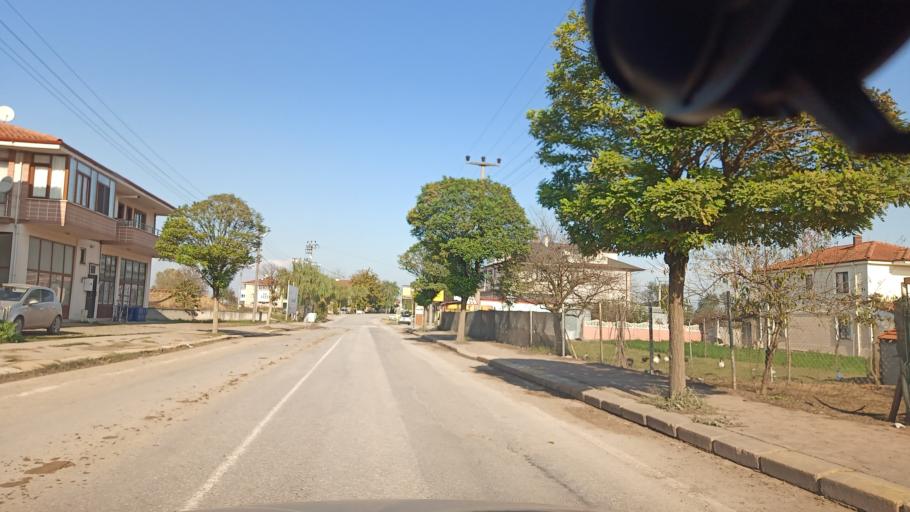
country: TR
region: Sakarya
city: Sogutlu
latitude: 40.8900
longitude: 30.4660
